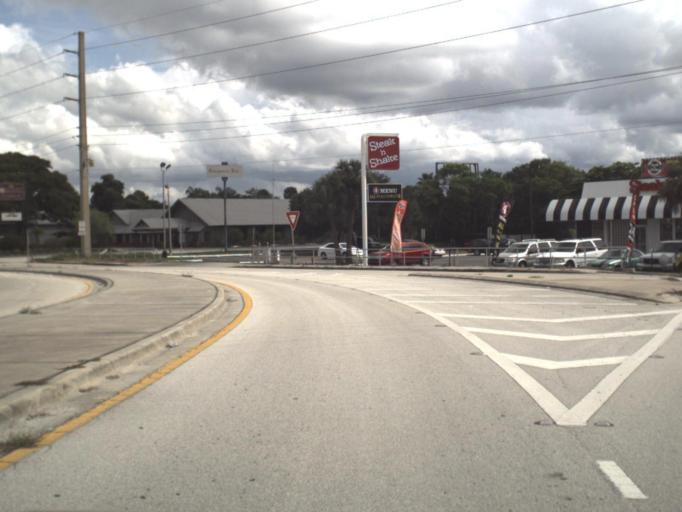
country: US
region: Florida
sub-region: Manatee County
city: West Samoset
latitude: 27.4627
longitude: -82.5633
